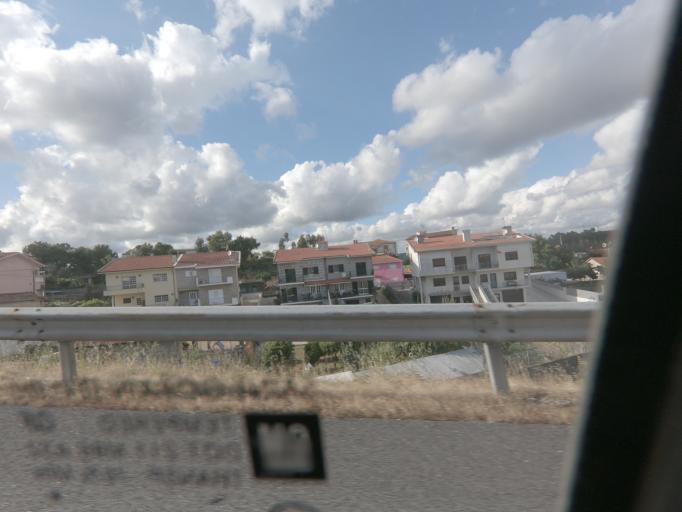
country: PT
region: Porto
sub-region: Valongo
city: Campo
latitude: 41.1877
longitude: -8.4636
